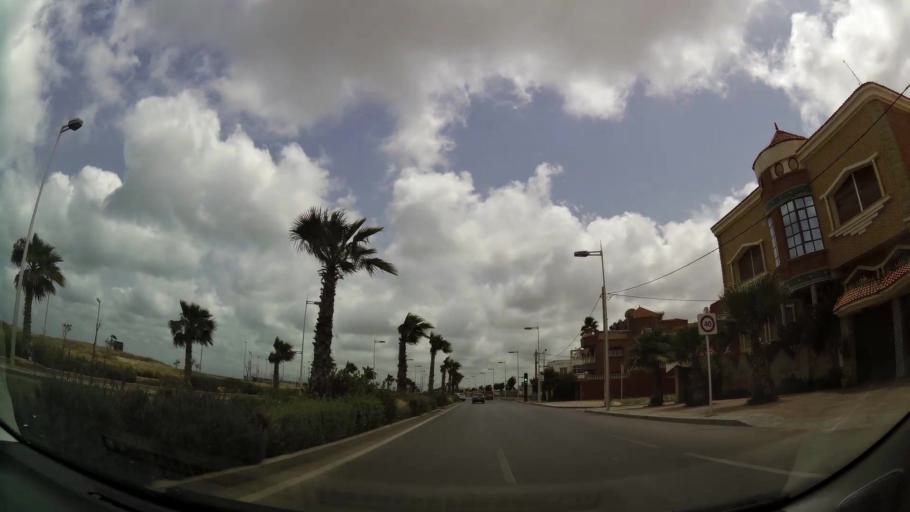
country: MA
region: Oriental
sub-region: Nador
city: Nador
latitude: 35.1678
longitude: -2.9135
